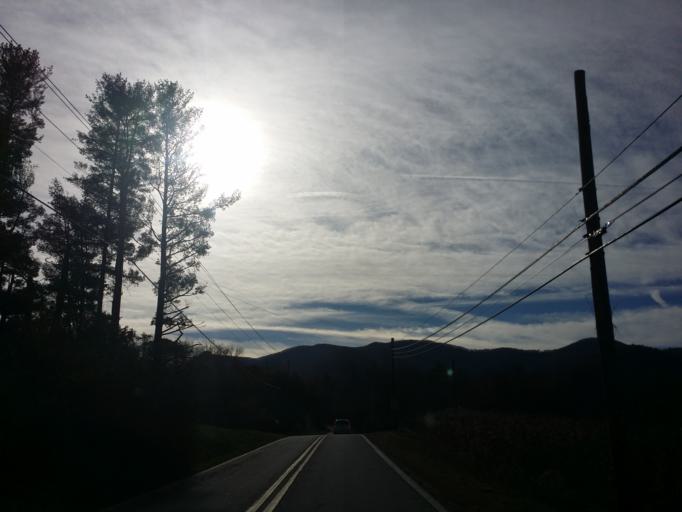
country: US
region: North Carolina
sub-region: Buncombe County
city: Swannanoa
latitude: 35.6104
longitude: -82.4150
